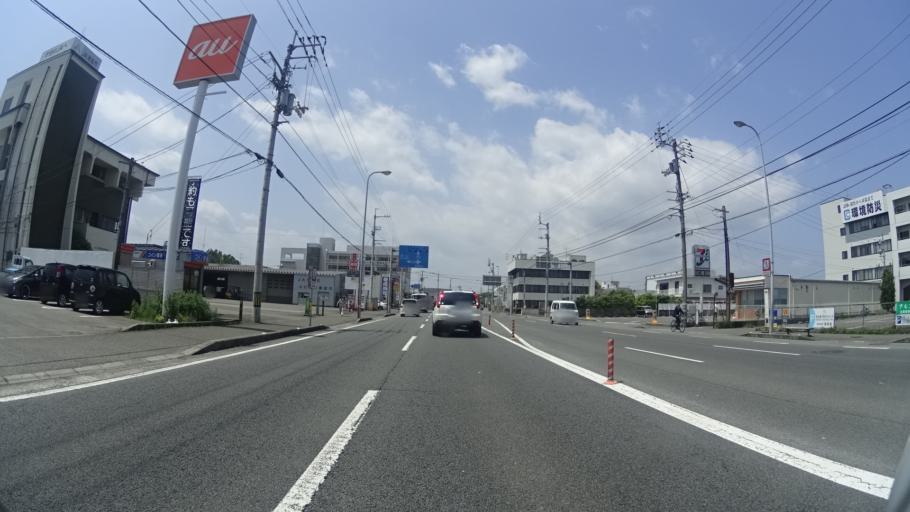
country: JP
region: Tokushima
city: Tokushima-shi
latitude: 34.0720
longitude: 134.5044
